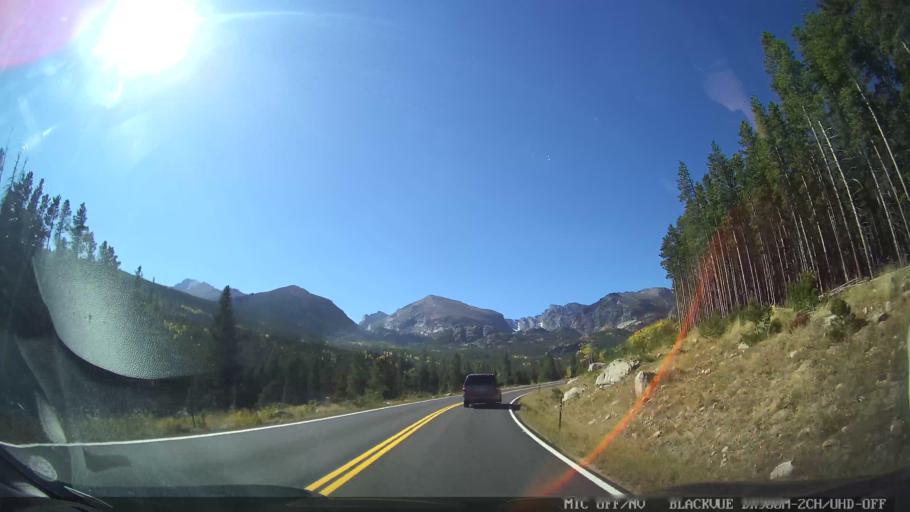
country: US
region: Colorado
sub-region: Larimer County
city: Estes Park
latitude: 40.3184
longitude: -105.6284
